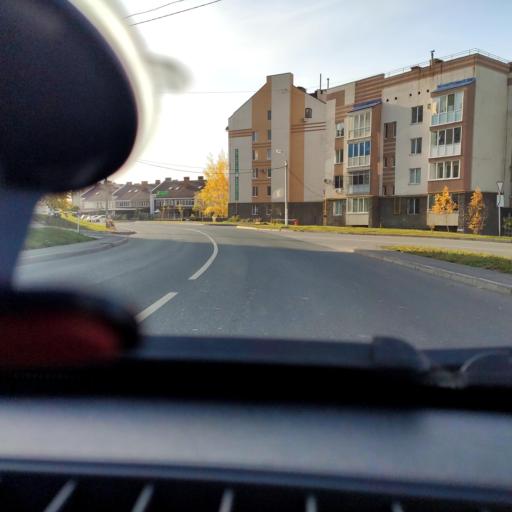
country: RU
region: Bashkortostan
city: Ufa
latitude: 54.6956
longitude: 55.9822
